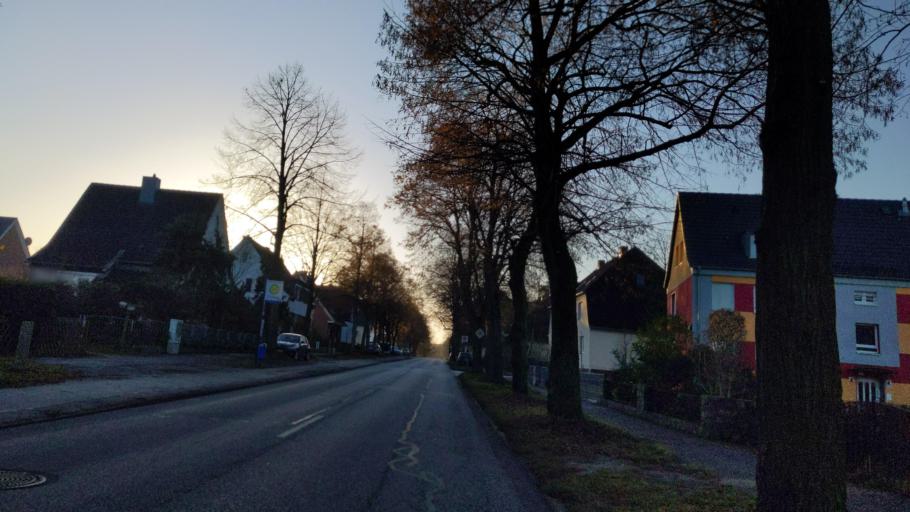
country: DE
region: Mecklenburg-Vorpommern
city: Selmsdorf
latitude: 53.8825
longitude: 10.7826
